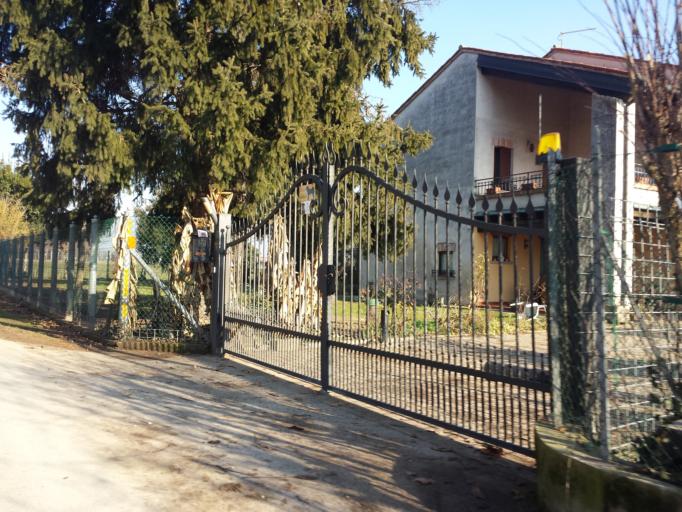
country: IT
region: Veneto
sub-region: Provincia di Vicenza
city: Sandrigo
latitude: 45.6451
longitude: 11.5974
